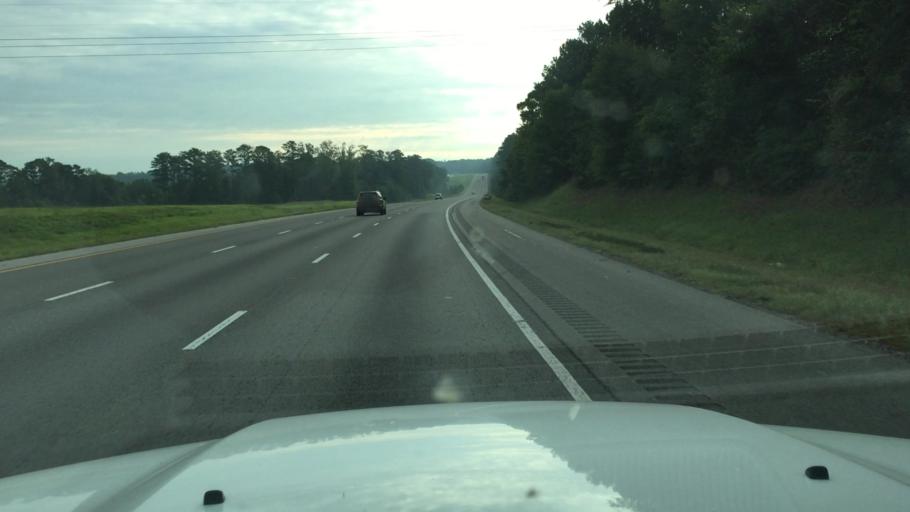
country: US
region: Alabama
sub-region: Tuscaloosa County
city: Coaling
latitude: 33.1830
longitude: -87.3622
